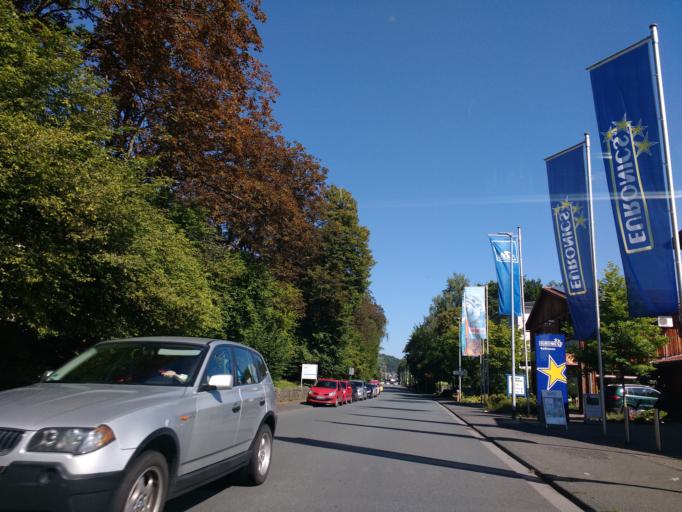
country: DE
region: Hesse
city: Herborn
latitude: 50.6722
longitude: 8.3053
